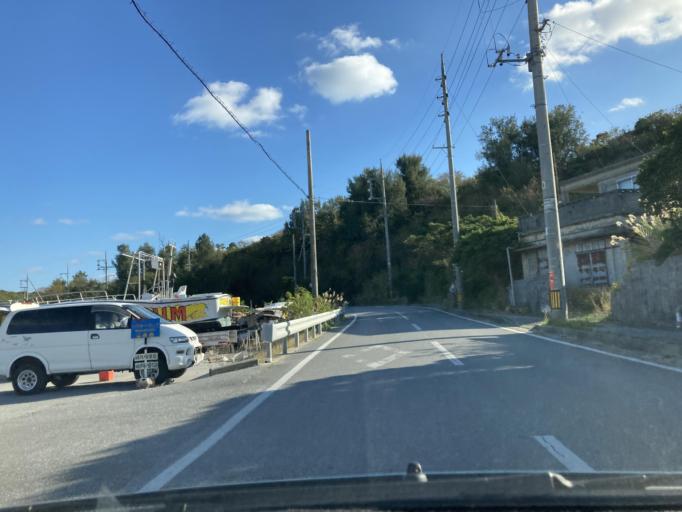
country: JP
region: Okinawa
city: Katsuren-haebaru
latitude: 26.3199
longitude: 127.9153
